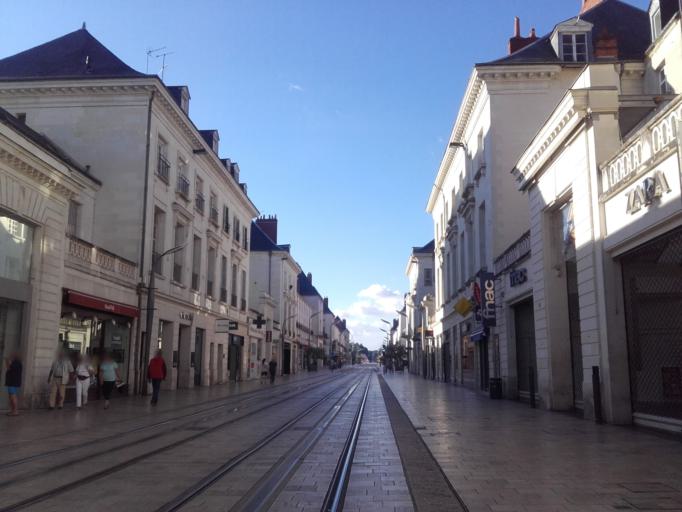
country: FR
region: Centre
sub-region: Departement d'Indre-et-Loire
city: Tours
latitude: 47.3922
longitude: 0.6880
